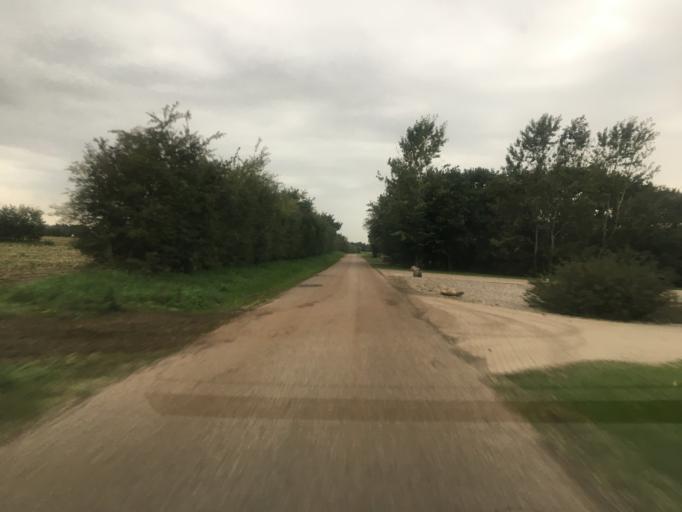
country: DE
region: Schleswig-Holstein
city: Ellhoft
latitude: 54.9535
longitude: 8.9821
